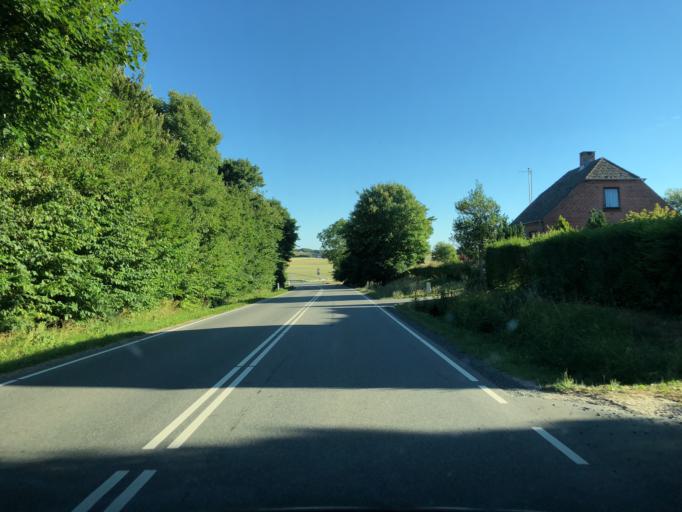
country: DK
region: Central Jutland
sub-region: Skanderborg Kommune
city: Stilling
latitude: 56.0941
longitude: 9.9701
